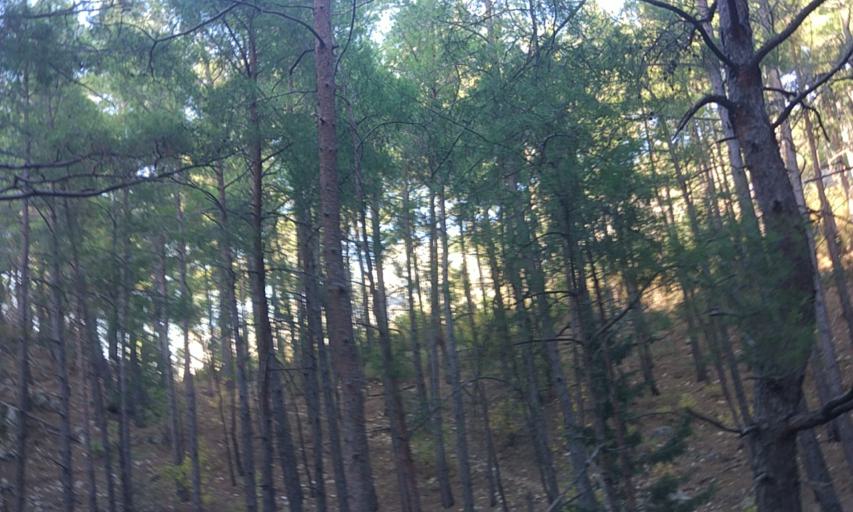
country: TR
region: Antalya
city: Tekirova
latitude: 36.3640
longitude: 30.4799
